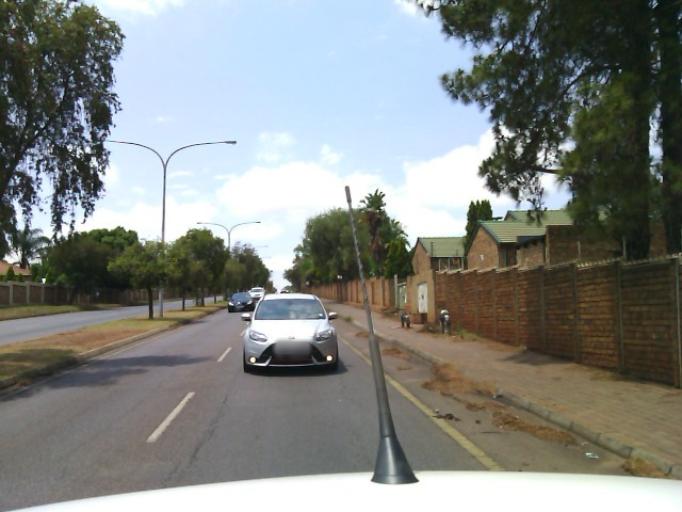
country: ZA
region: Gauteng
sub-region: City of Tshwane Metropolitan Municipality
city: Centurion
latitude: -25.8396
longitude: 28.1889
